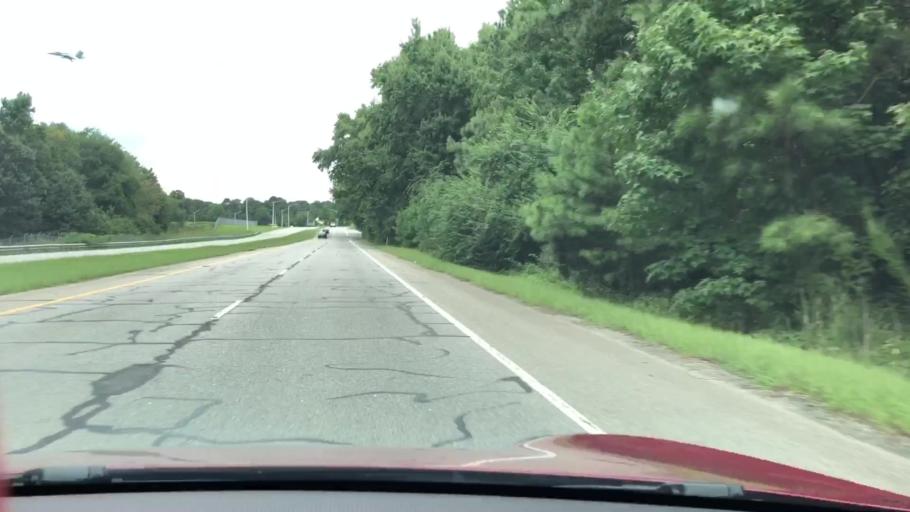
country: US
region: Virginia
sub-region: City of Virginia Beach
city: Virginia Beach
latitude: 36.8334
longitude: -76.0120
